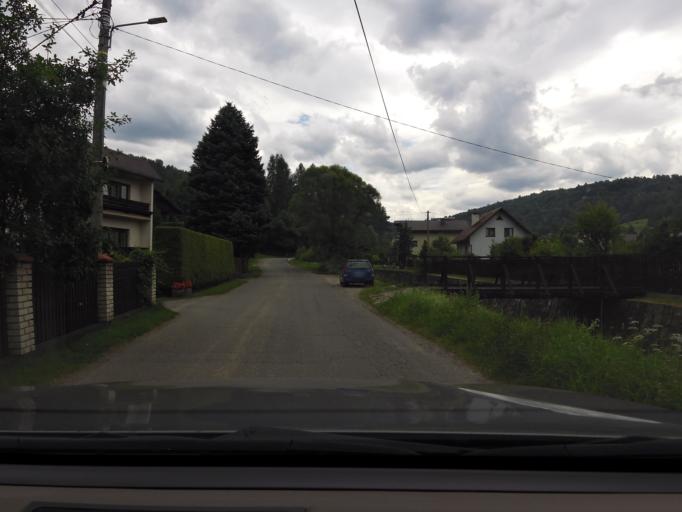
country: PL
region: Silesian Voivodeship
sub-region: Powiat zywiecki
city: Rajcza
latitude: 49.5076
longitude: 19.1122
